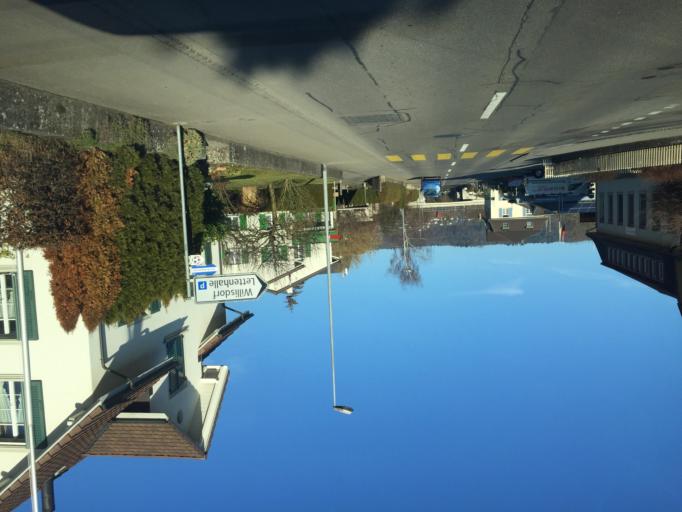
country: CH
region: Thurgau
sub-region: Frauenfeld District
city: Diessenhofen
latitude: 47.6846
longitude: 8.7502
